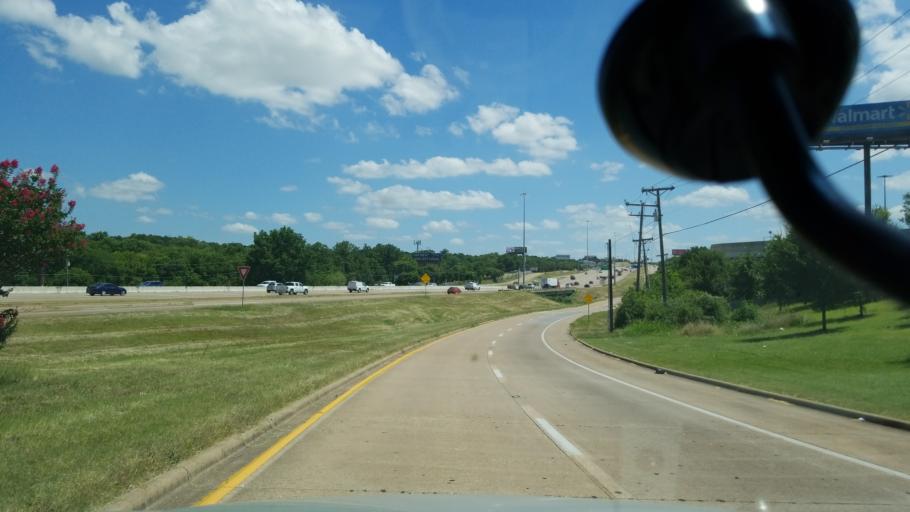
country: US
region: Texas
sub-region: Dallas County
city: Cockrell Hill
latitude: 32.6849
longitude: -96.8238
